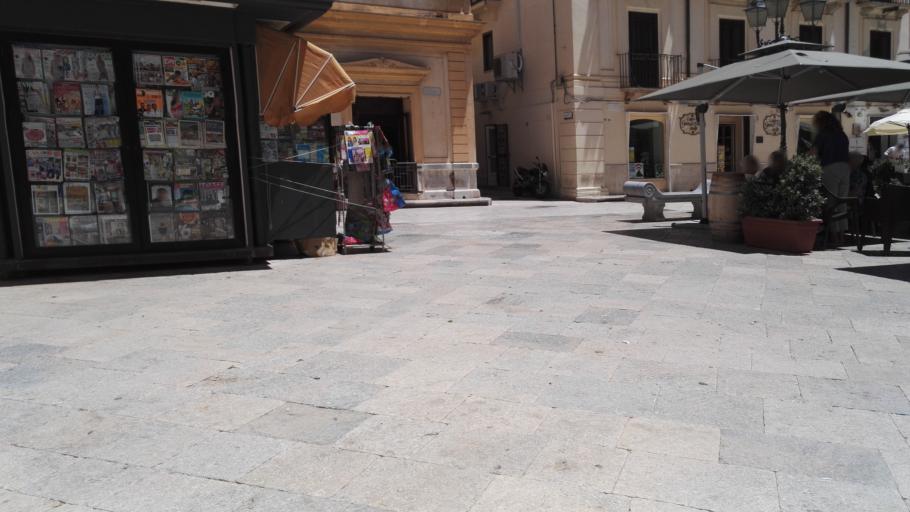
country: IT
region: Sicily
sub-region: Trapani
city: Marsala
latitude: 37.7995
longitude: 12.4345
